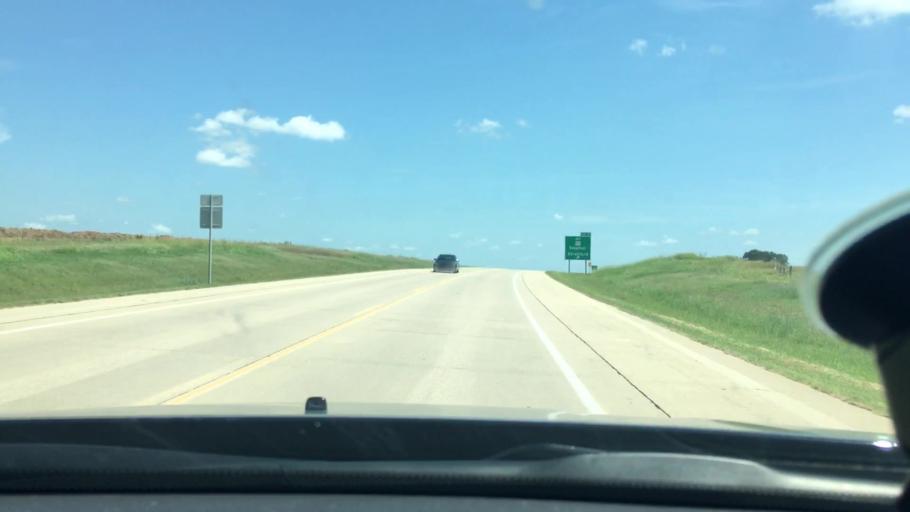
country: US
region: Oklahoma
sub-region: Murray County
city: Sulphur
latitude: 34.5433
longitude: -96.9773
